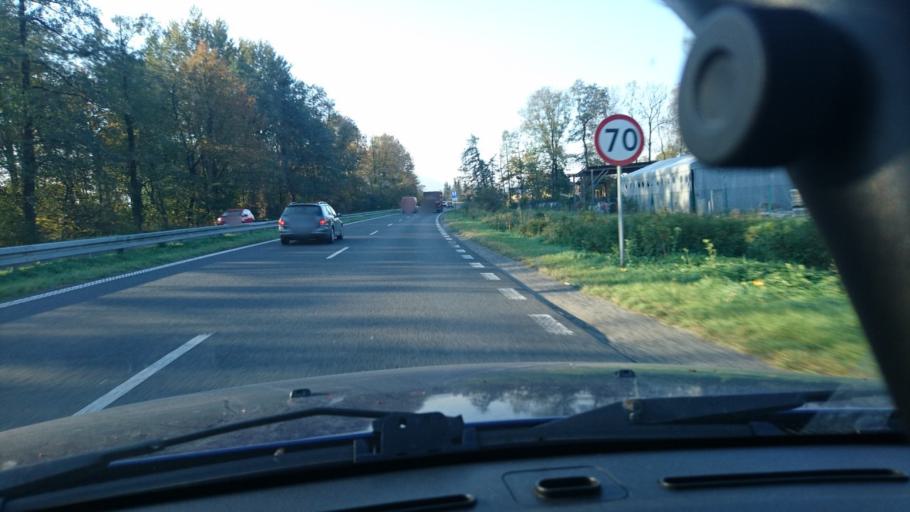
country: PL
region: Silesian Voivodeship
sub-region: Powiat cieszynski
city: Gorki Wielkie
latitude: 49.7630
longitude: 18.8088
